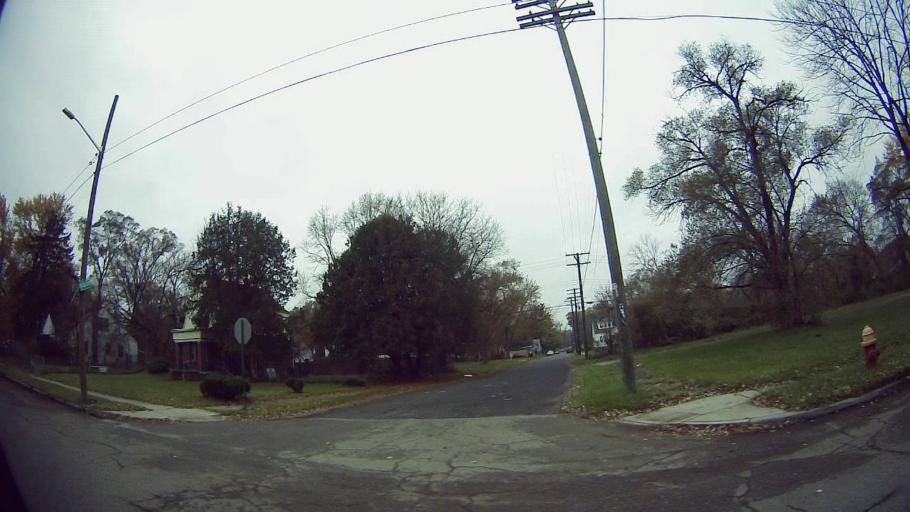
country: US
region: Michigan
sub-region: Oakland County
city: Southfield
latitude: 42.4175
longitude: -83.2383
